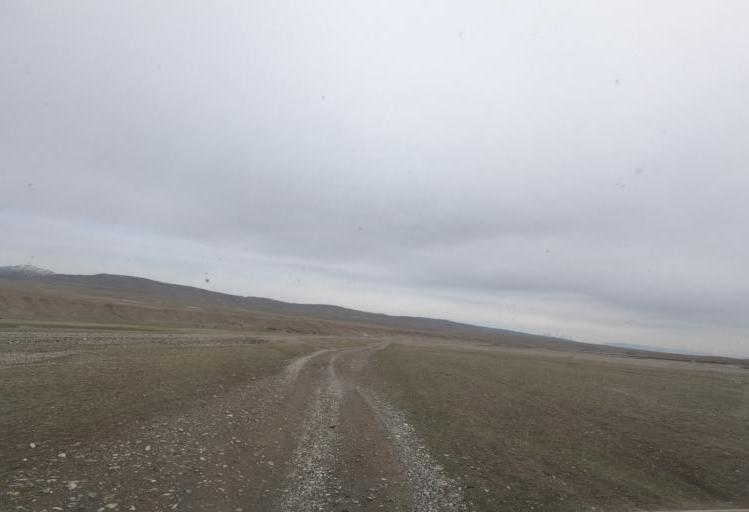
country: KG
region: Naryn
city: Baetov
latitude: 40.9303
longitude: 75.2783
